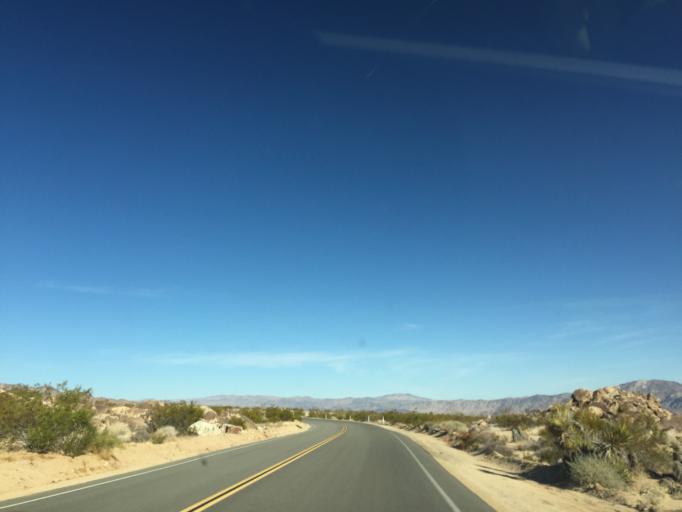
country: US
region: California
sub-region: Riverside County
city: Mecca
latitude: 33.8334
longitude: -115.7636
